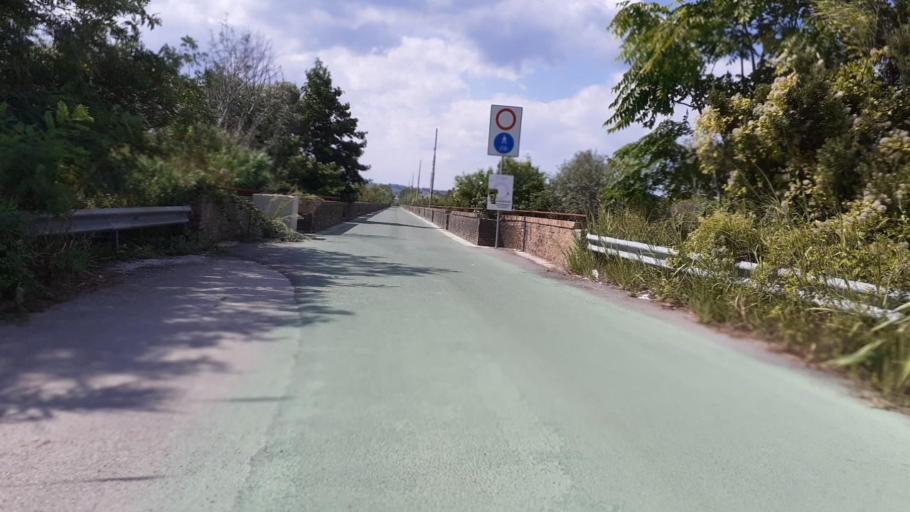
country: IT
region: Abruzzo
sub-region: Provincia di Chieti
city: Torino di Sangro
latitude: 42.2342
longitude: 14.5420
